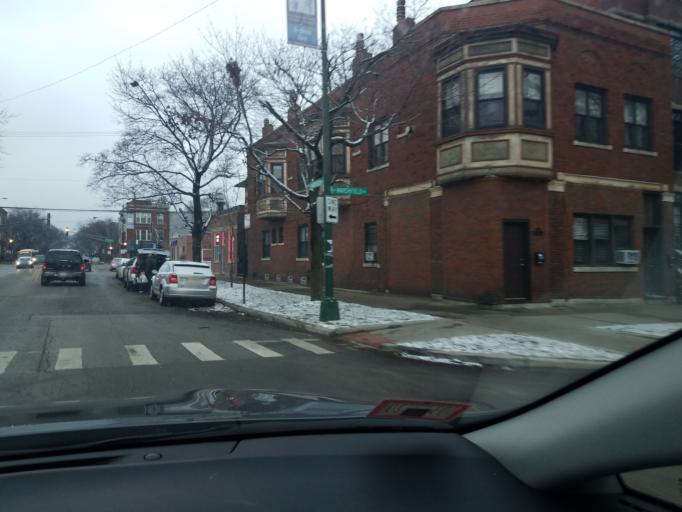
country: US
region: Illinois
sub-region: Cook County
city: Lincolnwood
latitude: 41.9470
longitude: -87.6701
